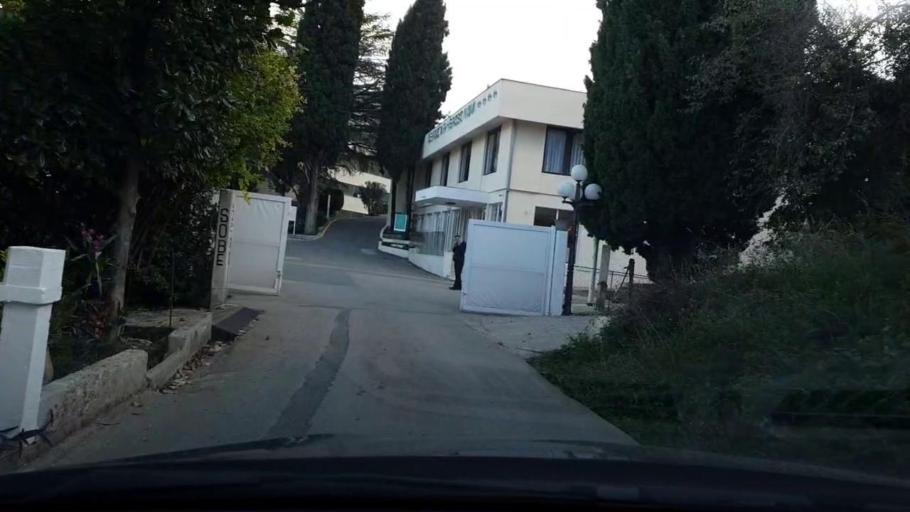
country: ME
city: Igalo
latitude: 42.4353
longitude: 18.5151
